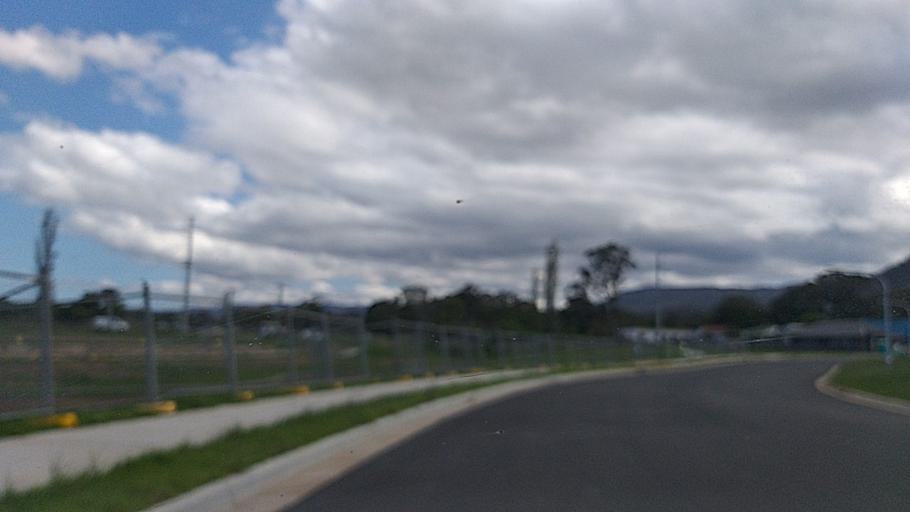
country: AU
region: New South Wales
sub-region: Wollongong
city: Dapto
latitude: -34.4775
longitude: 150.7662
